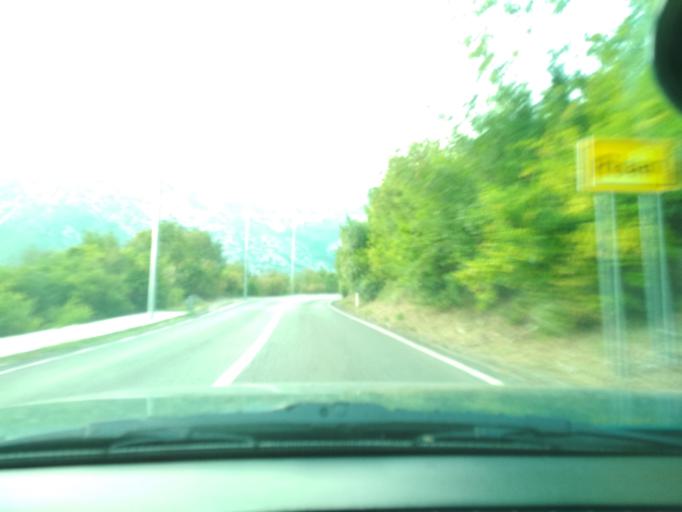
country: ME
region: Kotor
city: Risan
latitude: 42.4948
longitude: 18.6914
